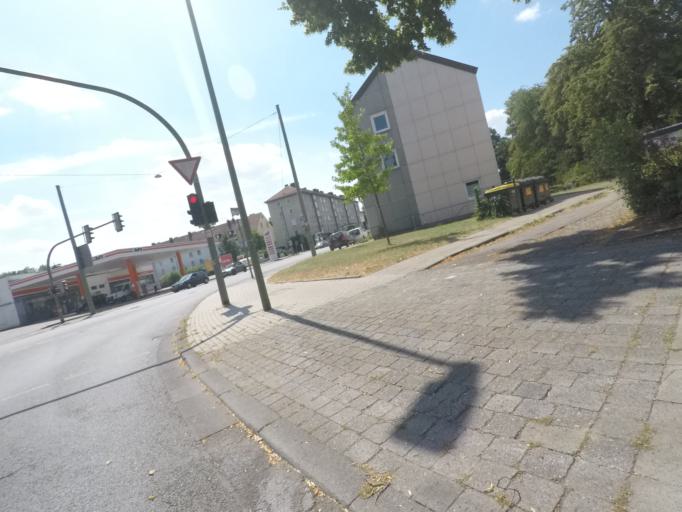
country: DE
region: North Rhine-Westphalia
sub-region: Regierungsbezirk Detmold
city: Bielefeld
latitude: 52.0287
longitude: 8.5759
